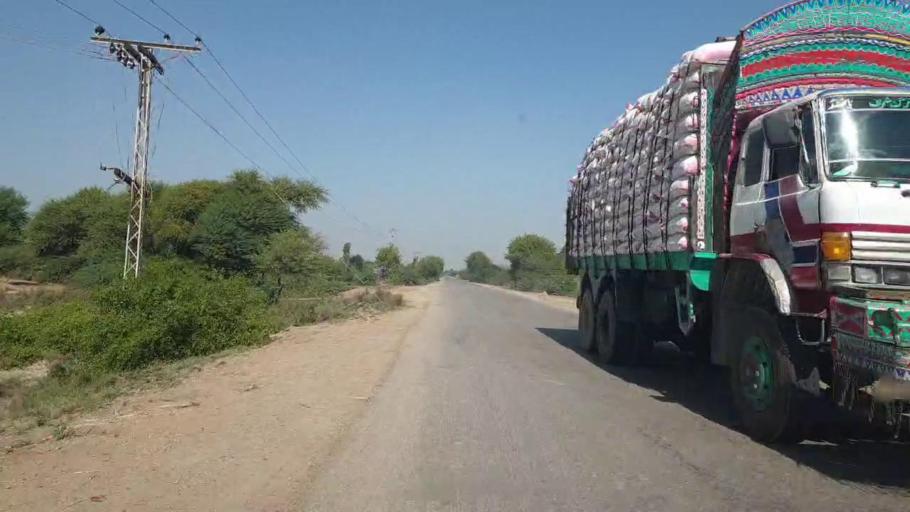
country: PK
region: Sindh
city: Talhar
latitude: 24.9135
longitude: 68.8577
